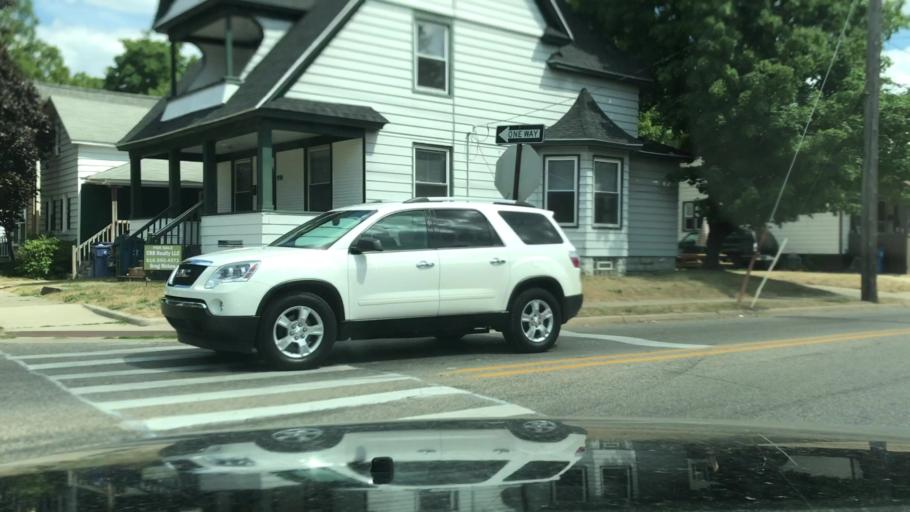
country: US
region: Michigan
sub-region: Kent County
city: Grand Rapids
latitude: 42.9721
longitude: -85.6926
